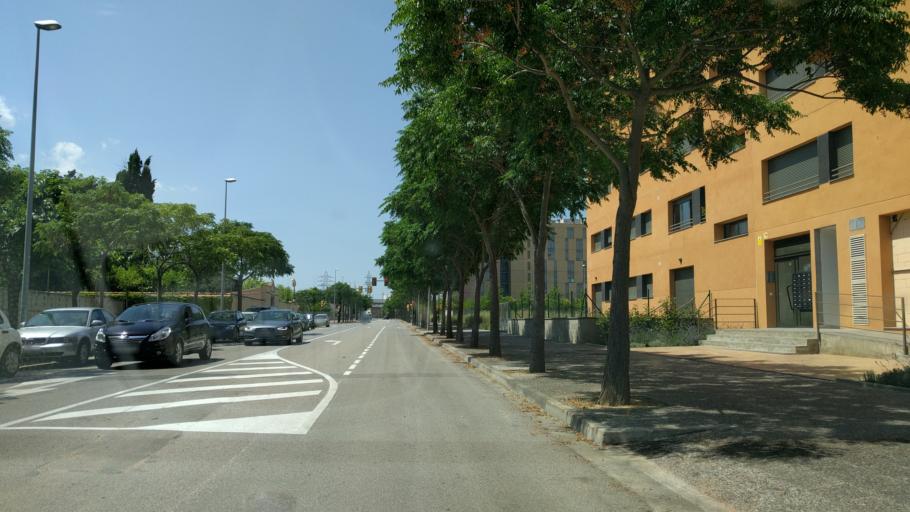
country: ES
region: Catalonia
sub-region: Provincia de Girona
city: Salt
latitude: 41.9724
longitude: 2.8041
